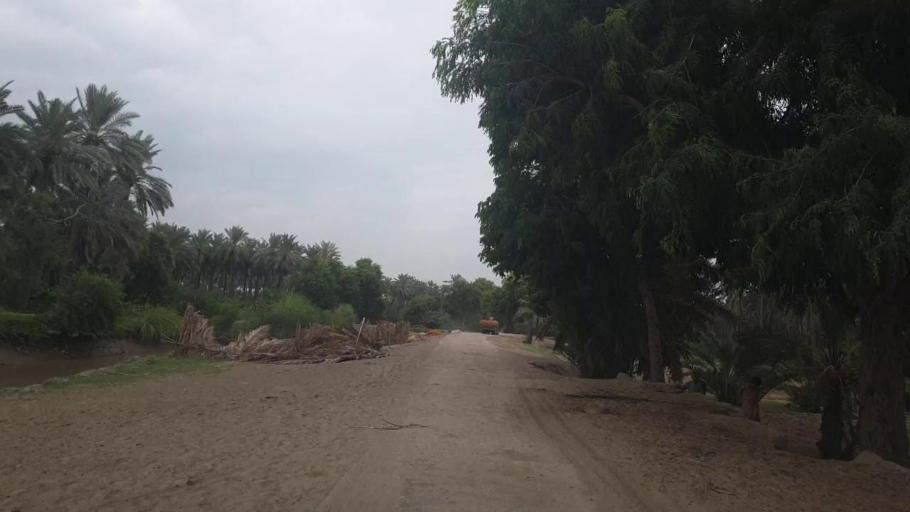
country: PK
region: Sindh
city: Khairpur
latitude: 27.6037
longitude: 68.7611
